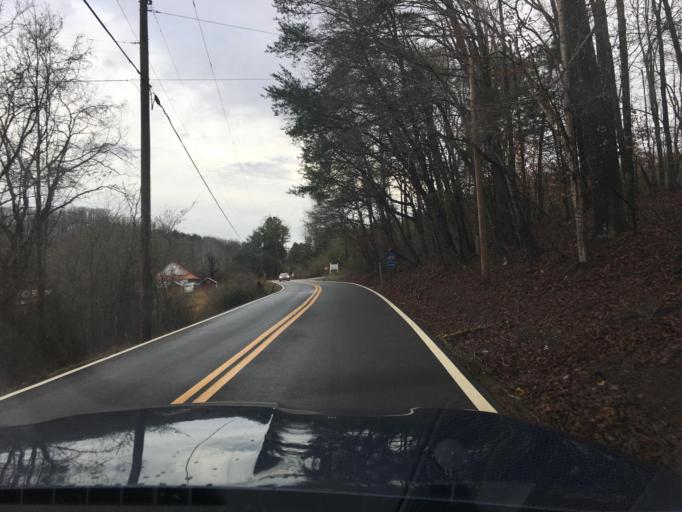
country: US
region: Tennessee
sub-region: McMinn County
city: Englewood
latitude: 35.3844
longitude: -84.4386
